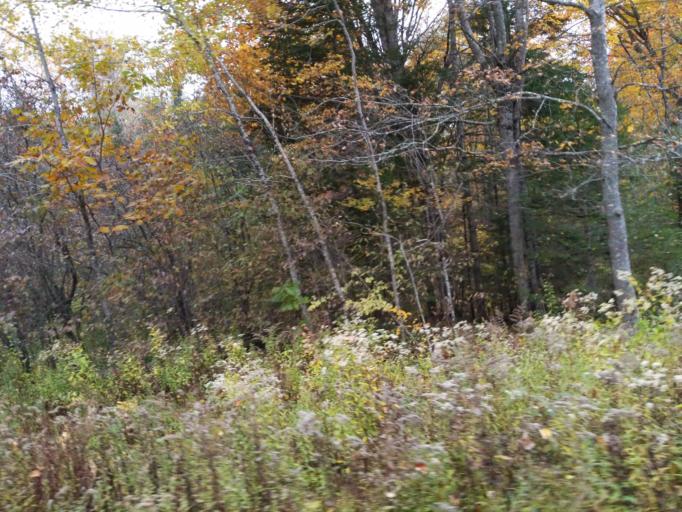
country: US
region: Maine
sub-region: Lincoln County
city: Wiscasset
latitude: 44.0808
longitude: -69.6237
